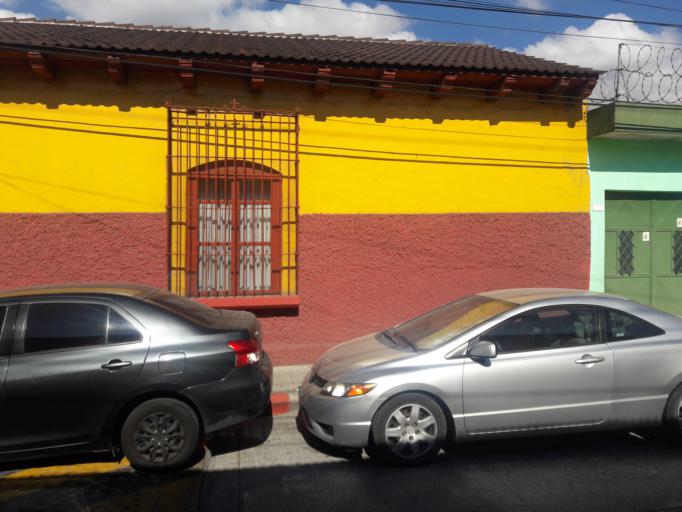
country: GT
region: Guatemala
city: Amatitlan
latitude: 14.4786
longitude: -90.6215
